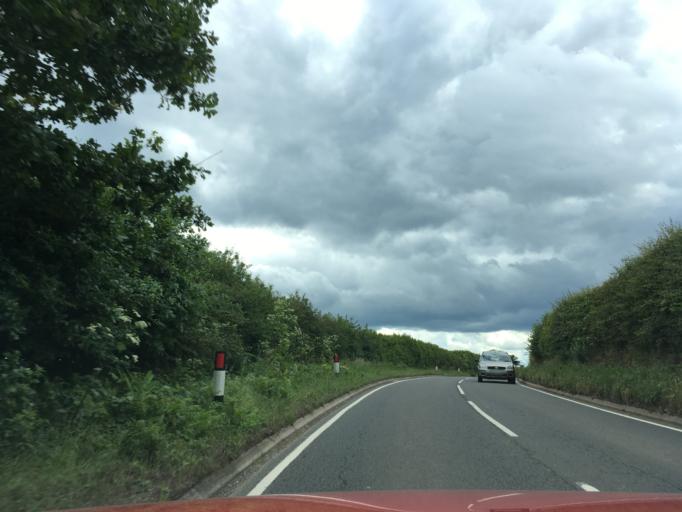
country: GB
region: England
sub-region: Central Bedfordshire
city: Woburn
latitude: 51.9800
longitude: -0.6381
